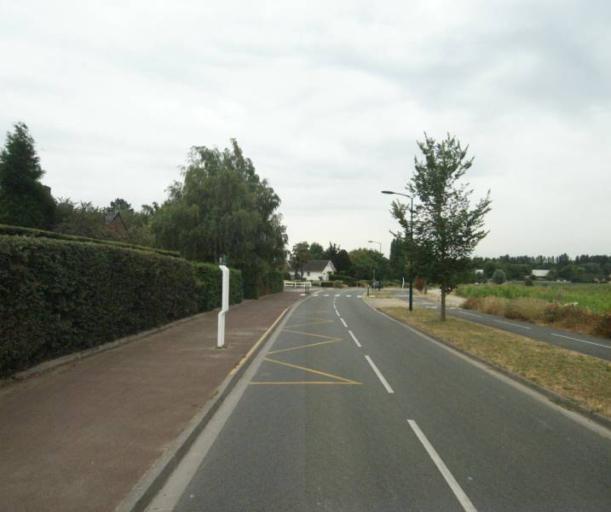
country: FR
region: Nord-Pas-de-Calais
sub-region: Departement du Nord
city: Bondues
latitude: 50.6987
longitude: 3.0878
